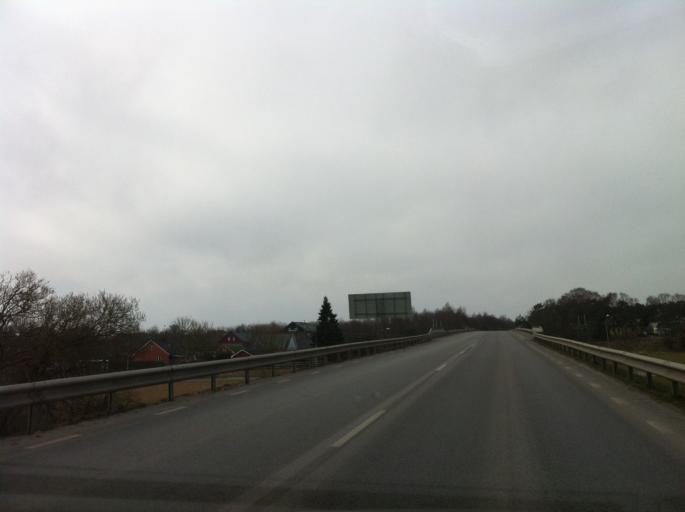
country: SE
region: Skane
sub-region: Kavlinge Kommun
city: Kaevlinge
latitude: 55.7916
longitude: 13.1311
